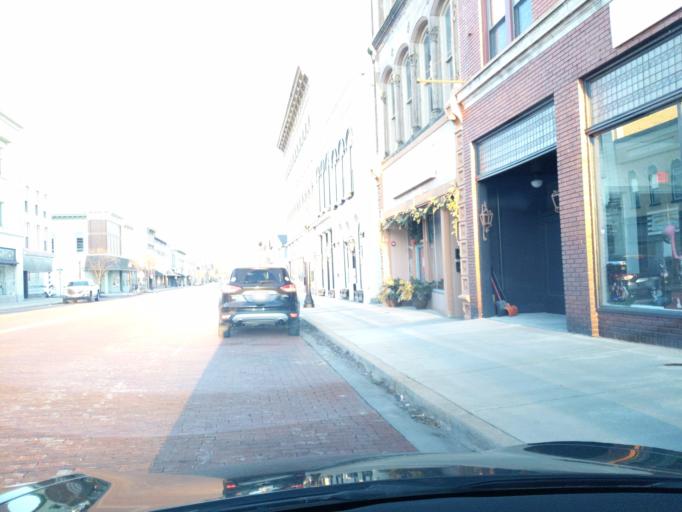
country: US
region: Michigan
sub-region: Ionia County
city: Ionia
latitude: 42.9823
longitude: -85.0687
